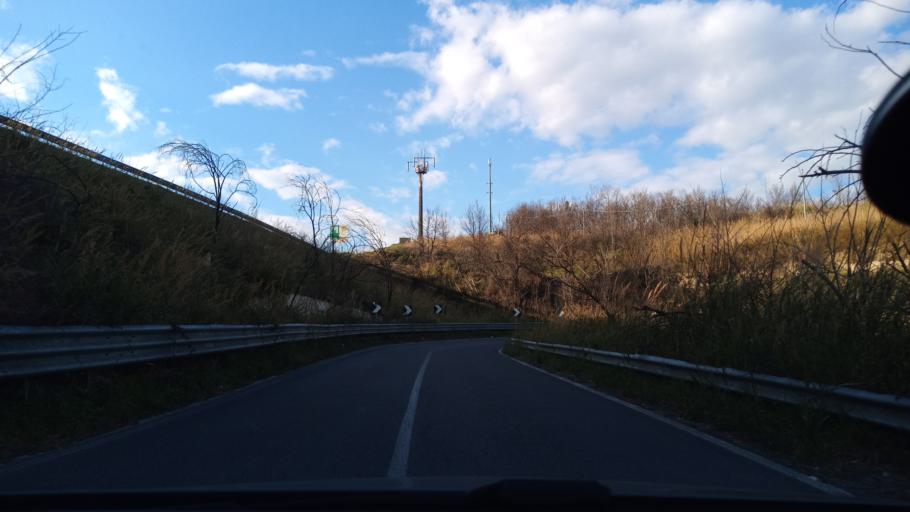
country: IT
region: Latium
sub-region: Citta metropolitana di Roma Capitale
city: Nazzano
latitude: 42.2060
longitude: 12.6042
